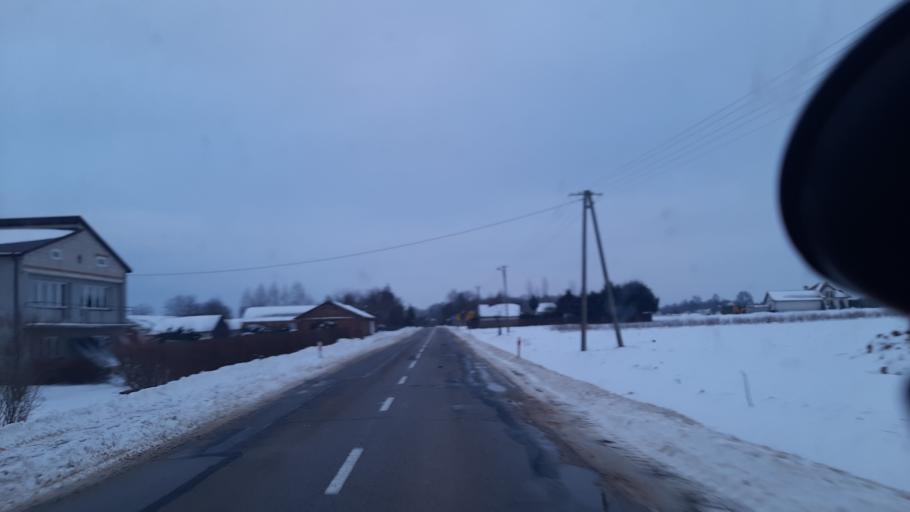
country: PL
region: Lublin Voivodeship
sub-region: Powiat lubelski
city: Jastkow
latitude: 51.3440
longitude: 22.4020
